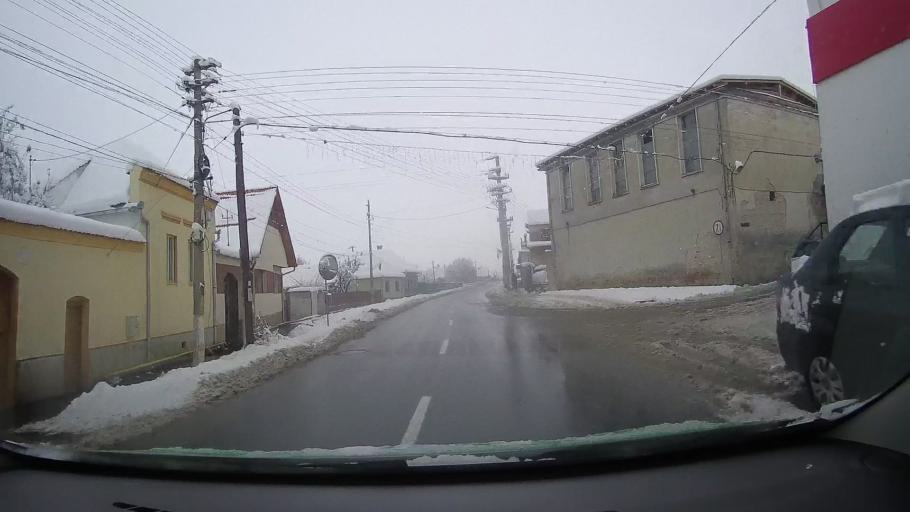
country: RO
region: Sibiu
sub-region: Comuna Orlat
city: Orlat
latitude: 45.7572
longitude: 23.9698
